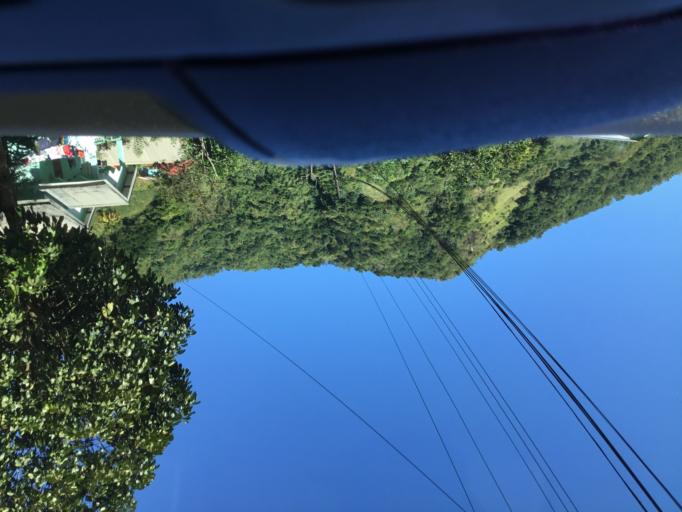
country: VC
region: Saint David
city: Chateaubelair
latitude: 13.2601
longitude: -61.2500
